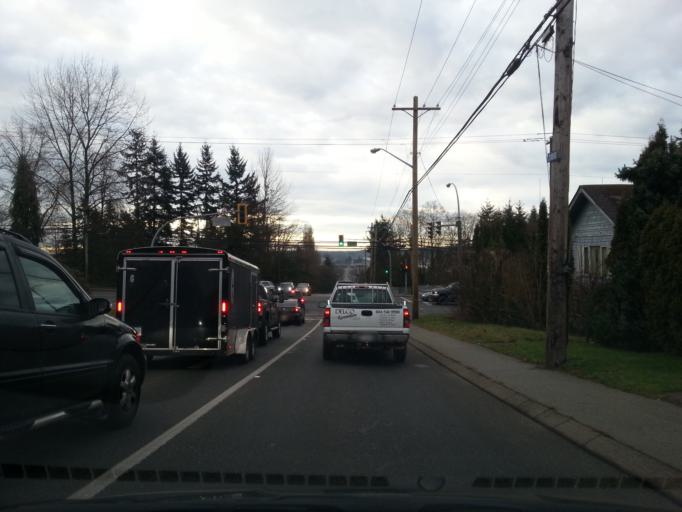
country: CA
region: British Columbia
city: Langley
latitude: 49.1046
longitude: -122.7128
